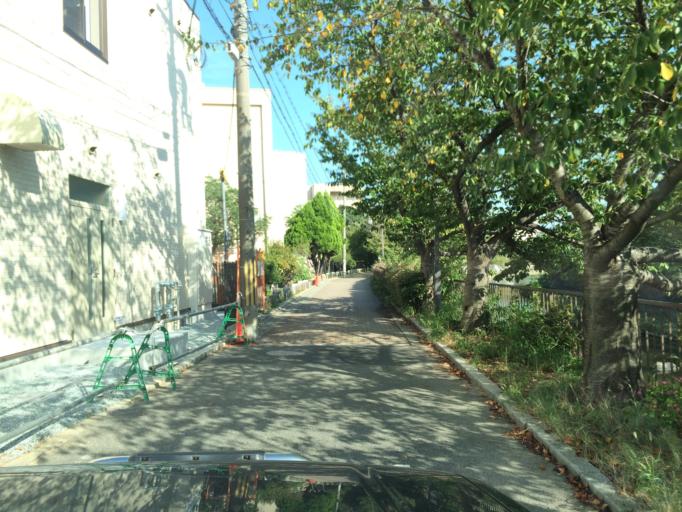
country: JP
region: Hyogo
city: Amagasaki
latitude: 34.7483
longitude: 135.4076
